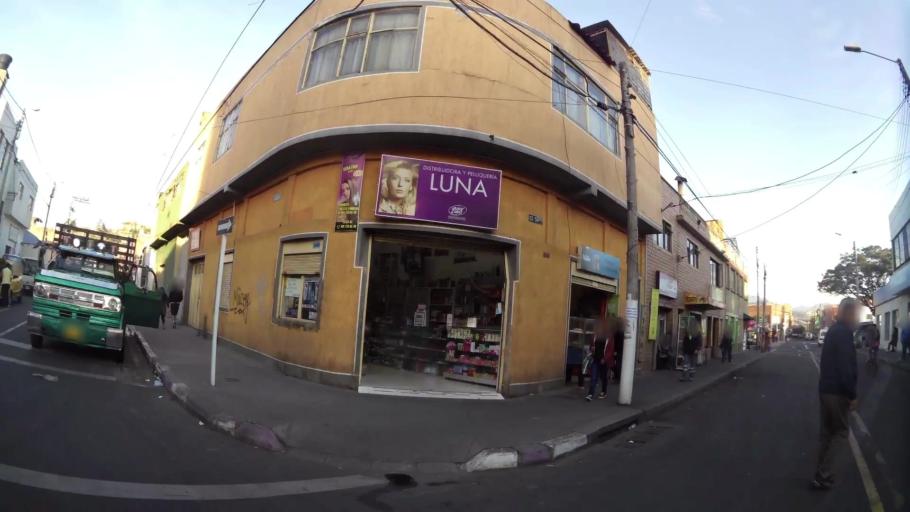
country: CO
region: Bogota D.C.
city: Bogota
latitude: 4.5628
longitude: -74.1278
